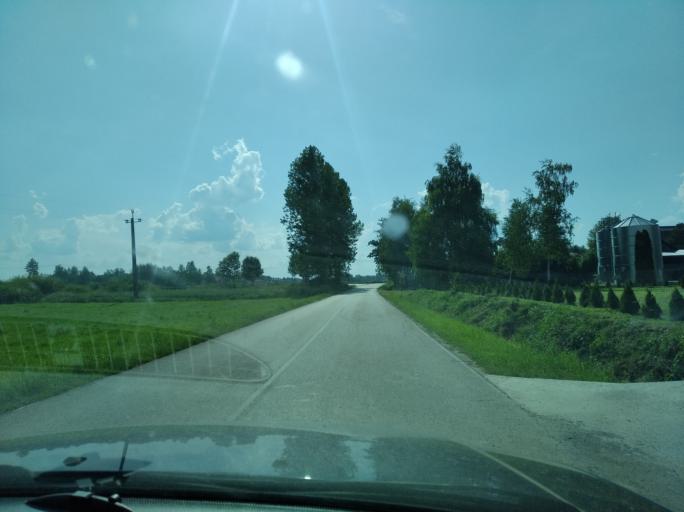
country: PL
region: Subcarpathian Voivodeship
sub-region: Powiat jaroslawski
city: Rokietnica
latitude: 49.9252
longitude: 22.7079
